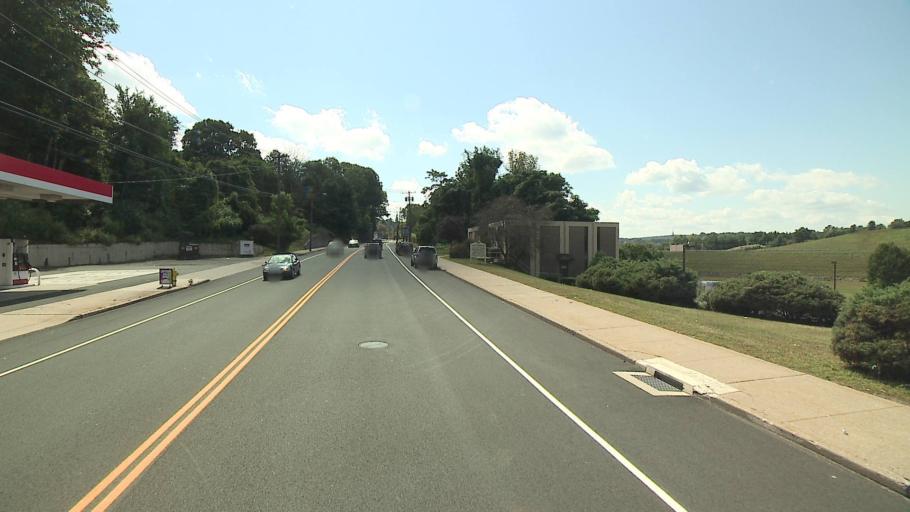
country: US
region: Connecticut
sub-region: New Haven County
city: Ansonia
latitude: 41.3354
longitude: -73.0761
